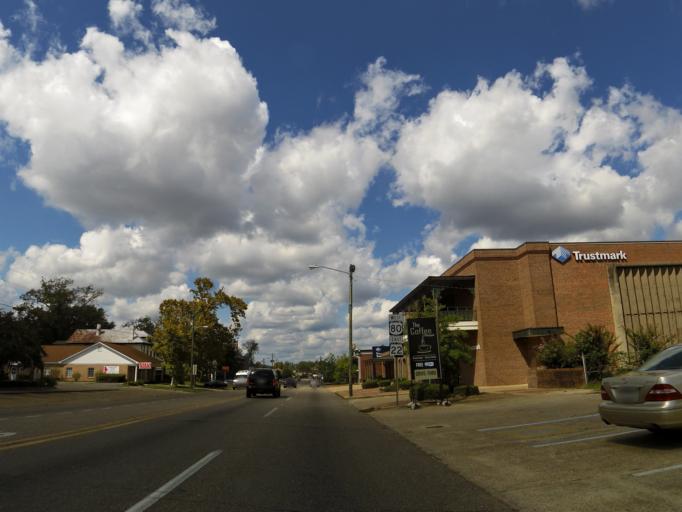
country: US
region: Alabama
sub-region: Dallas County
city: Selma
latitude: 32.4105
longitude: -87.0214
